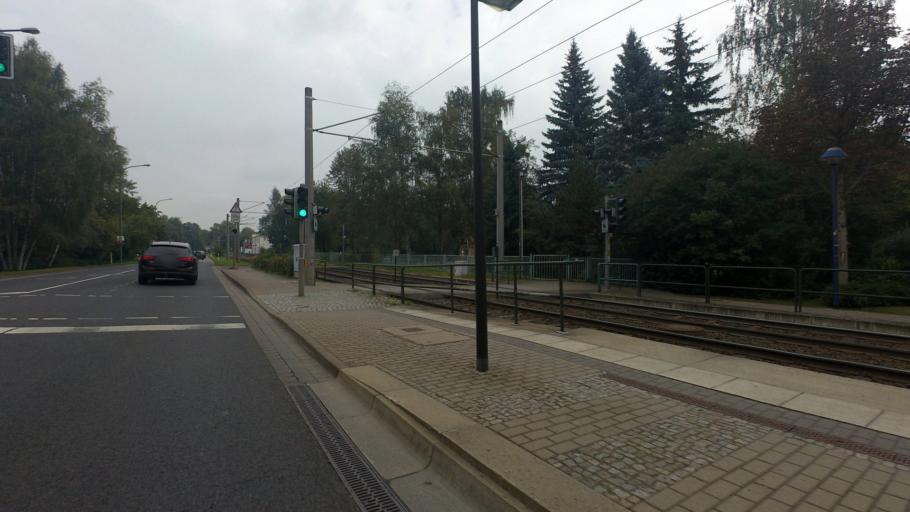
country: DE
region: Saxony
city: Albertstadt
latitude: 51.1237
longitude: 13.7914
